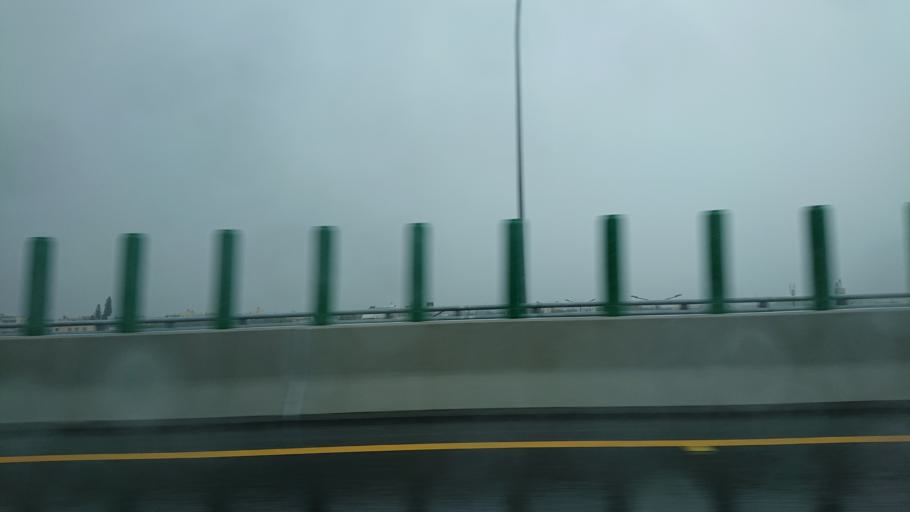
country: TW
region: Taiwan
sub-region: Changhua
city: Chang-hua
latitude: 23.9392
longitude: 120.3222
